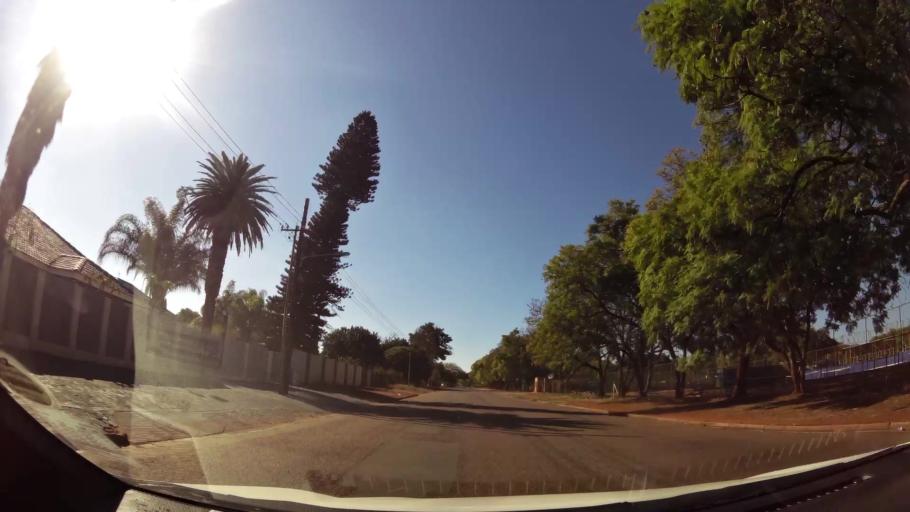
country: ZA
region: Limpopo
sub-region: Waterberg District Municipality
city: Mokopane
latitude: -24.1858
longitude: 29.0031
